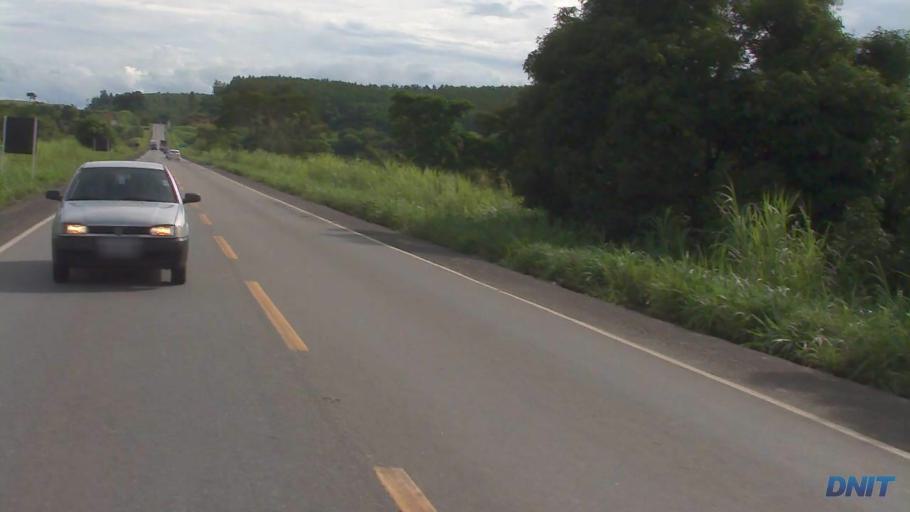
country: BR
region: Minas Gerais
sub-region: Belo Oriente
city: Belo Oriente
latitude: -19.2393
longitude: -42.3333
